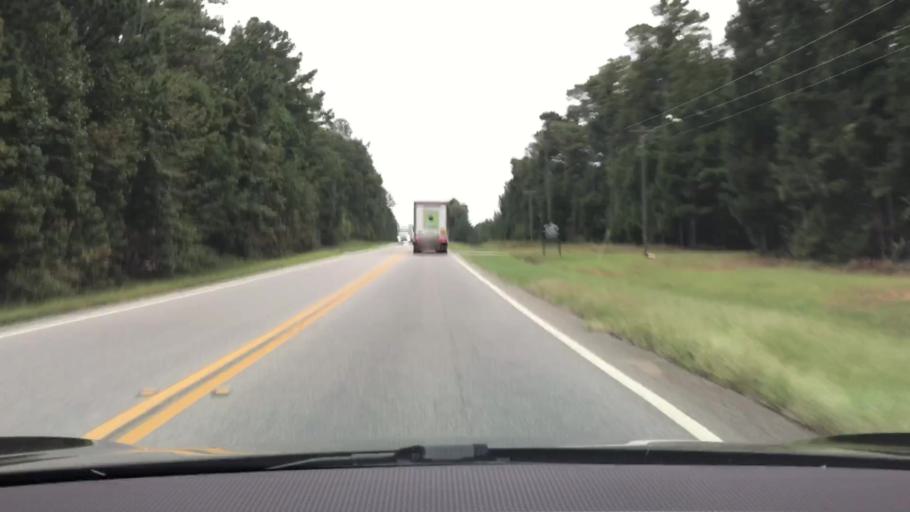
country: US
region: Georgia
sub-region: Greene County
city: Greensboro
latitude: 33.6582
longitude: -83.2402
